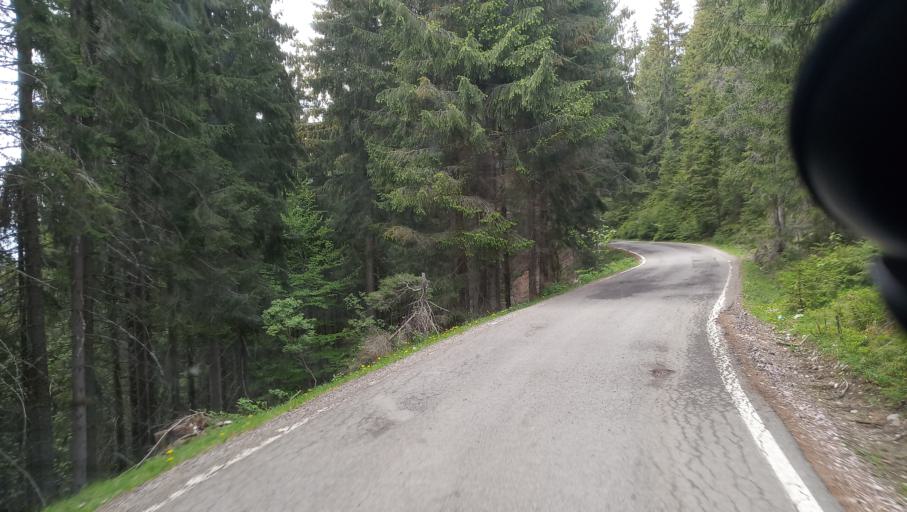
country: RO
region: Alba
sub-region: Comuna Horea
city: Horea
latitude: 46.5267
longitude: 22.8883
